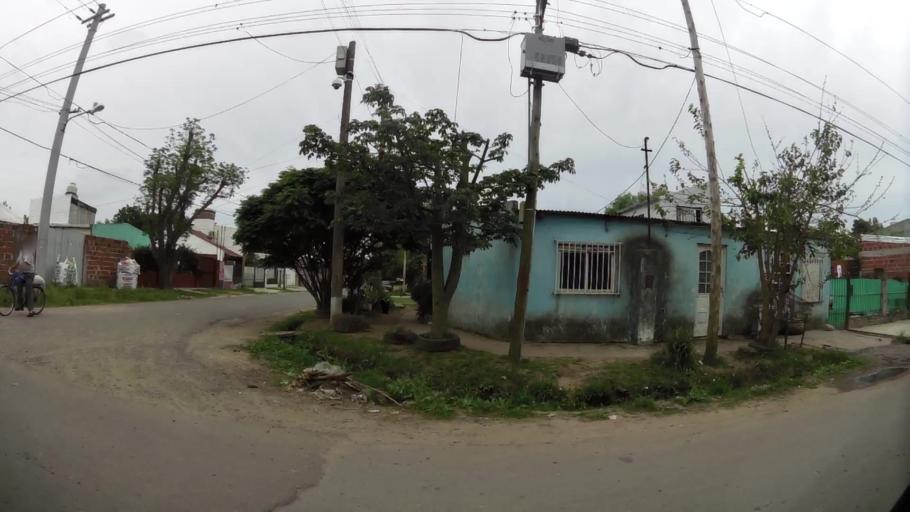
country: AR
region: Buenos Aires
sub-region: Partido de Campana
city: Campana
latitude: -34.1837
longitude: -58.9391
